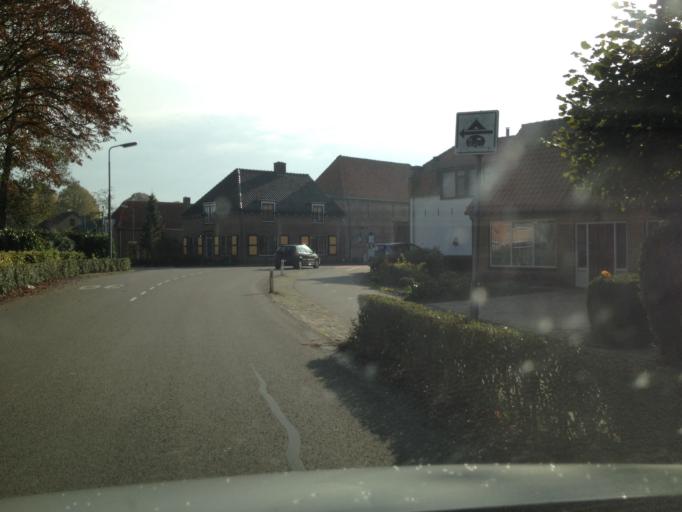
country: NL
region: Zeeland
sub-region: Gemeente Sluis
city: Sluis
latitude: 51.3128
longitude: 3.3877
